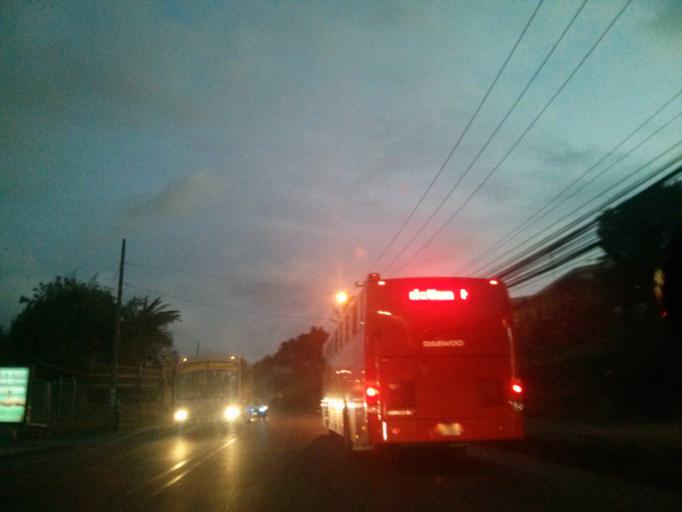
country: CR
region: San Jose
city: Colima
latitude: 9.9570
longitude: -84.1109
